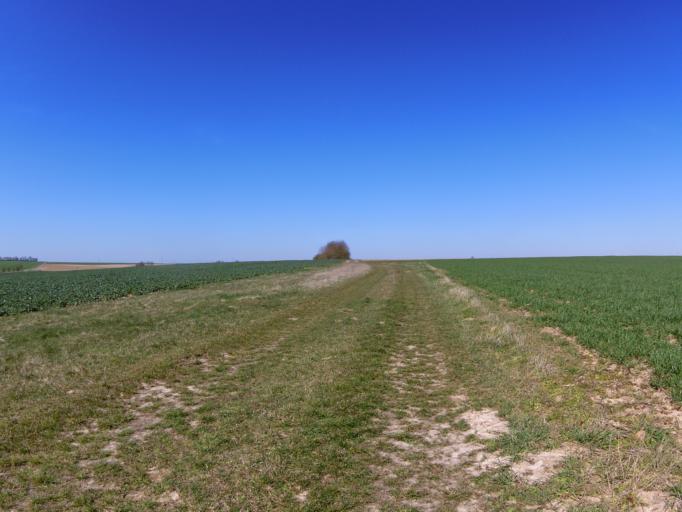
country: DE
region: Bavaria
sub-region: Regierungsbezirk Unterfranken
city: Prosselsheim
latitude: 49.8396
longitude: 10.1362
